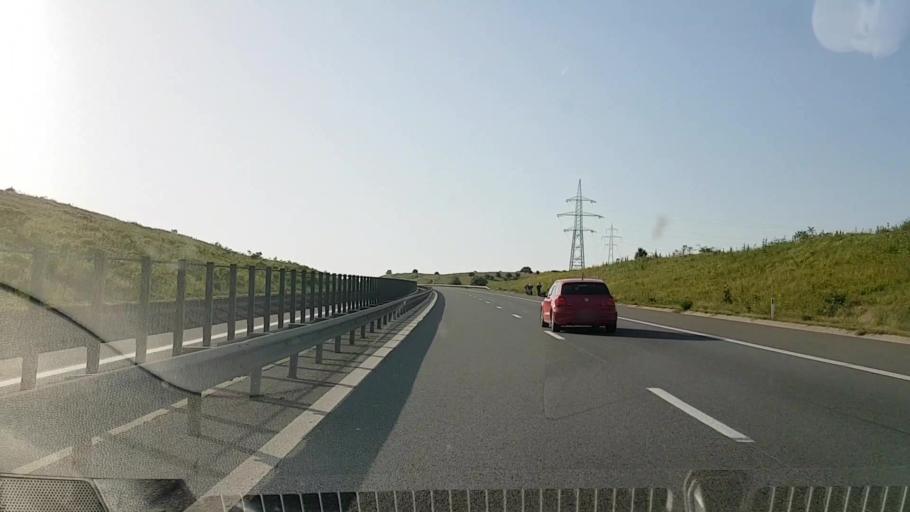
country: RO
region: Cluj
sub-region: Comuna Ciurila
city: Ciurila
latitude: 46.6488
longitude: 23.5133
